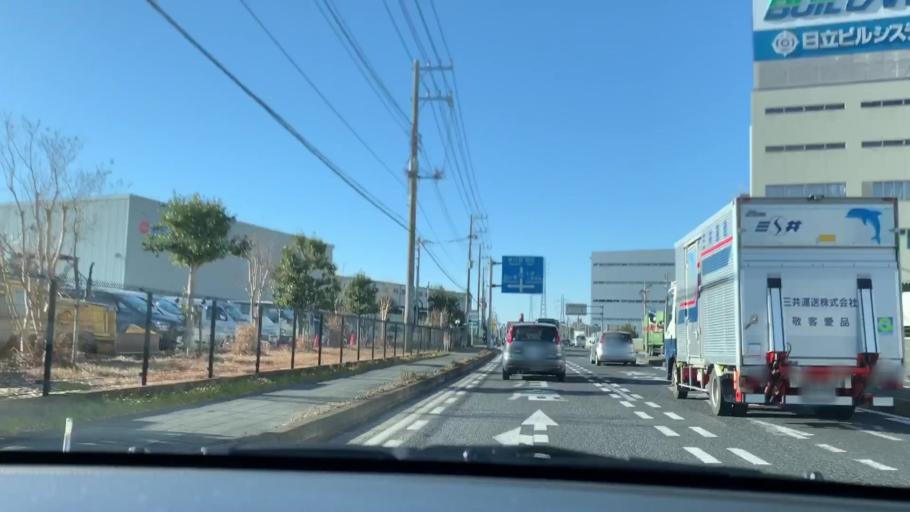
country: JP
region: Chiba
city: Kashiwa
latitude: 35.9046
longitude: 139.9476
